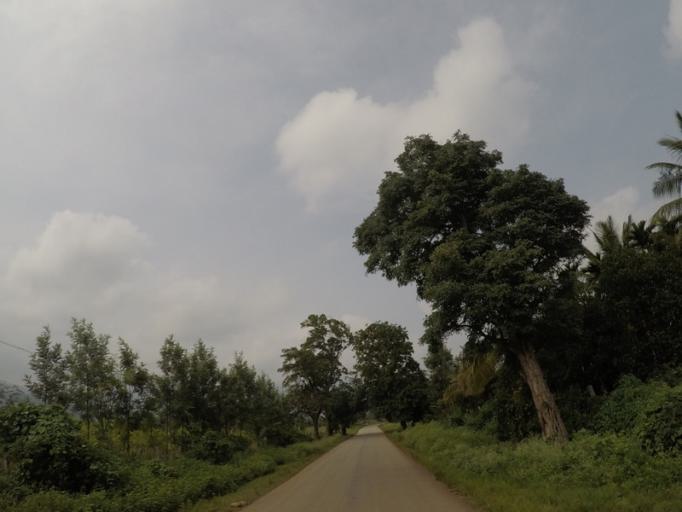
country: IN
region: Karnataka
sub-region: Chikmagalur
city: Tarikere
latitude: 13.5736
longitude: 75.8152
